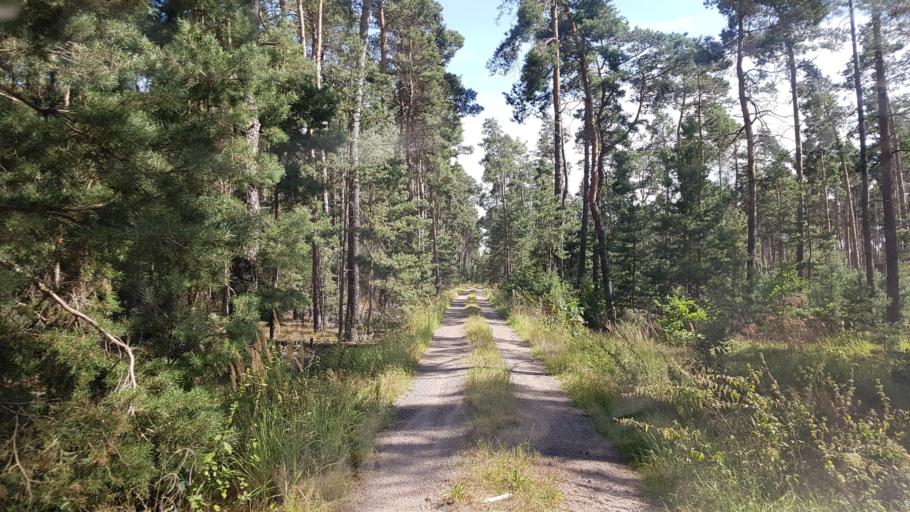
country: DE
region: Brandenburg
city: Bad Liebenwerda
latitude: 51.5001
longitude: 13.3000
